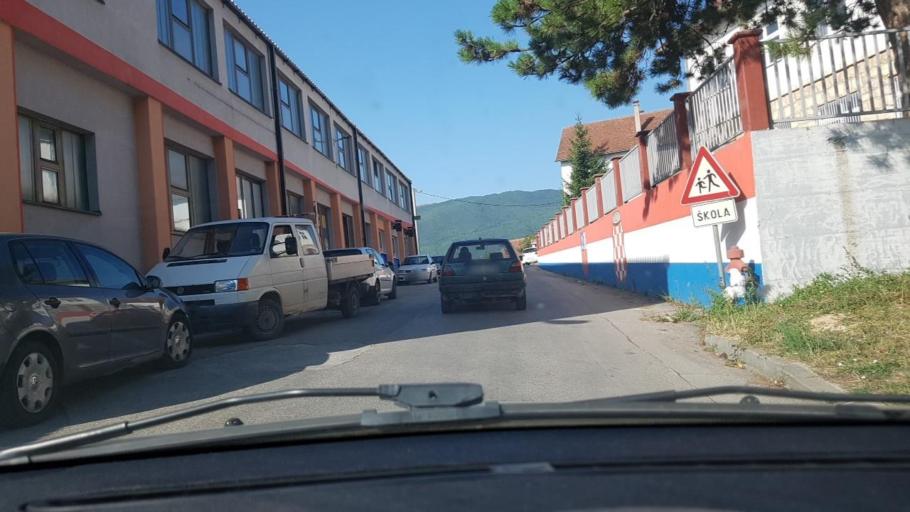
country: BA
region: Federation of Bosnia and Herzegovina
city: Rumboci
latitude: 43.8292
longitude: 17.5063
